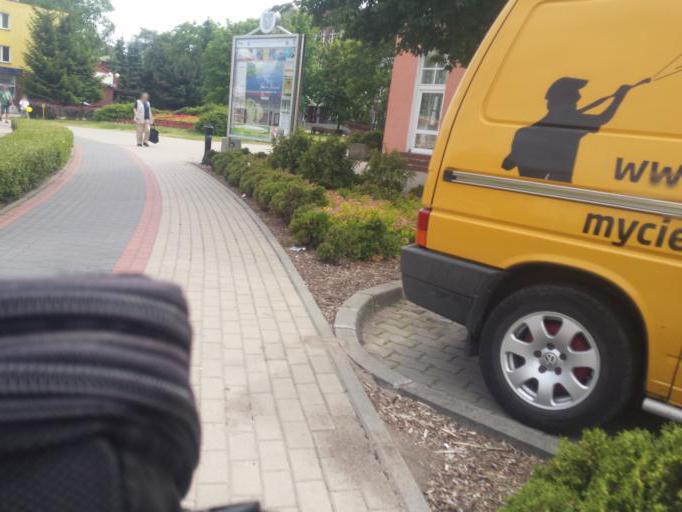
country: PL
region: Warmian-Masurian Voivodeship
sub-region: Powiat ilawski
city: Ilawa
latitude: 53.5975
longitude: 19.5615
